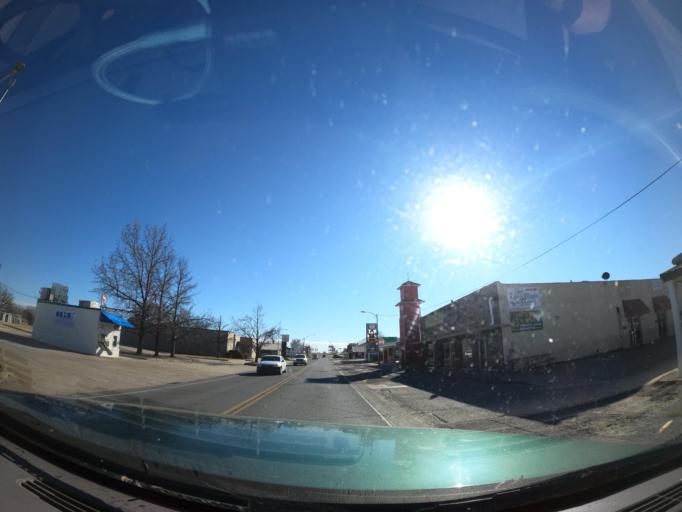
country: US
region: Oklahoma
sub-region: McIntosh County
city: Eufaula
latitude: 35.2854
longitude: -95.5826
